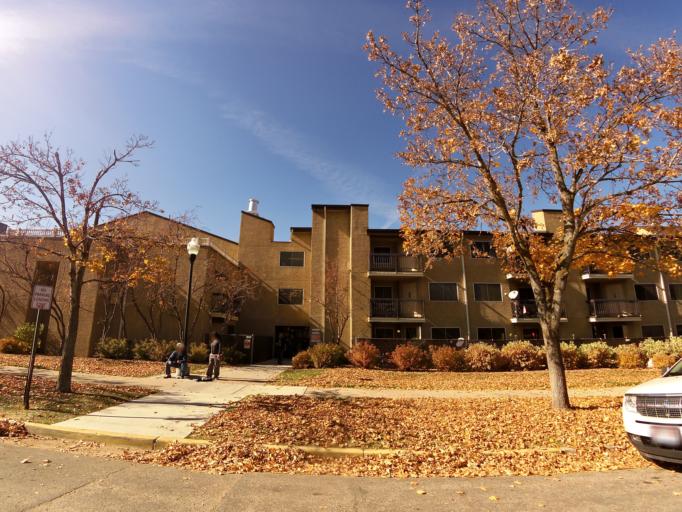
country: US
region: Utah
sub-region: Weber County
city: Ogden
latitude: 41.2218
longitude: -111.9649
